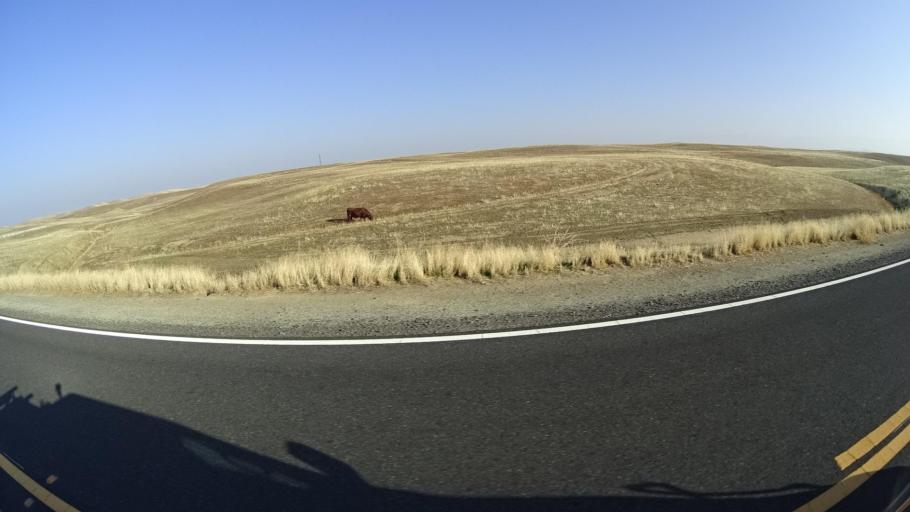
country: US
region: California
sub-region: Tulare County
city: Richgrove
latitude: 35.7513
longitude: -119.0051
